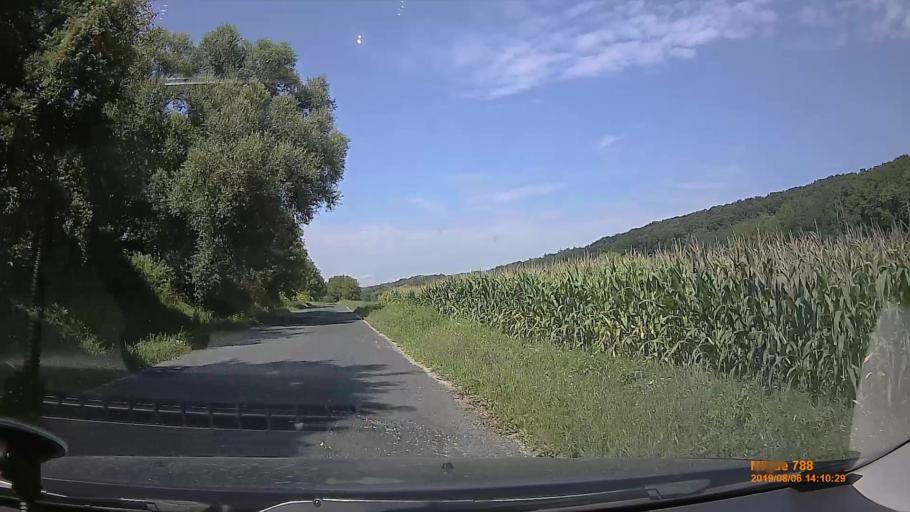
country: HU
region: Zala
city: Zalakomar
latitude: 46.5496
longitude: 17.0818
